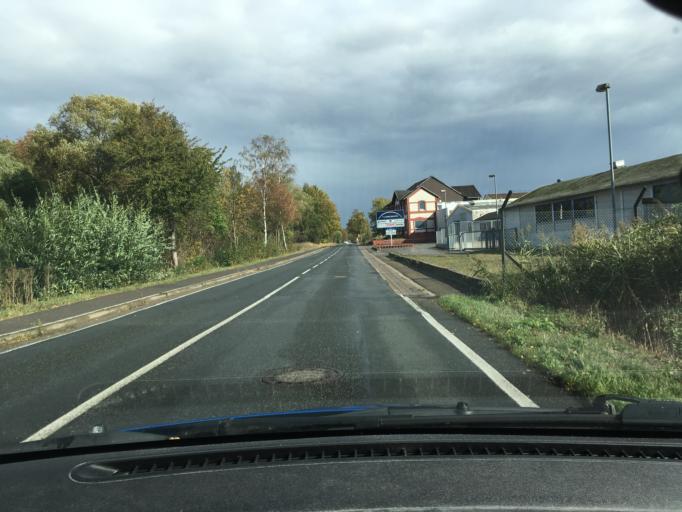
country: DE
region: Lower Saxony
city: Springe
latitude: 52.2110
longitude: 9.6202
